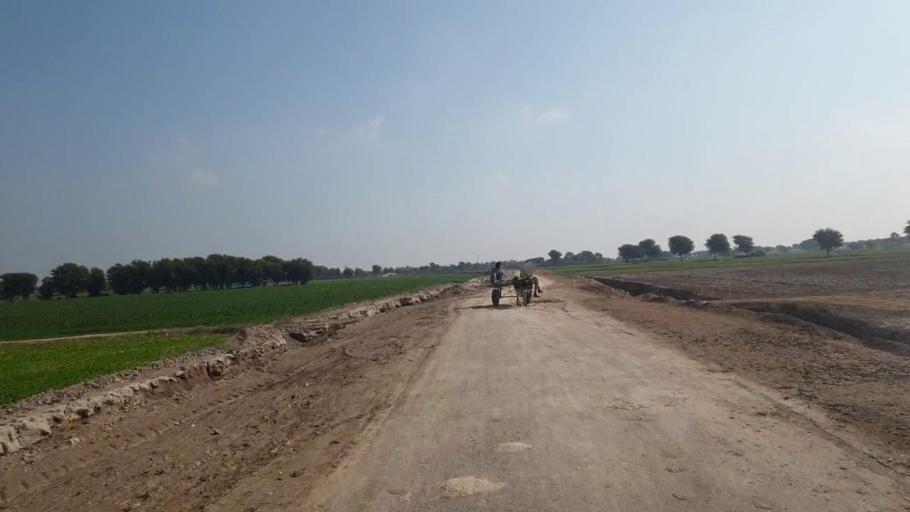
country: PK
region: Sindh
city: Shahdadpur
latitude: 26.0297
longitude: 68.6212
